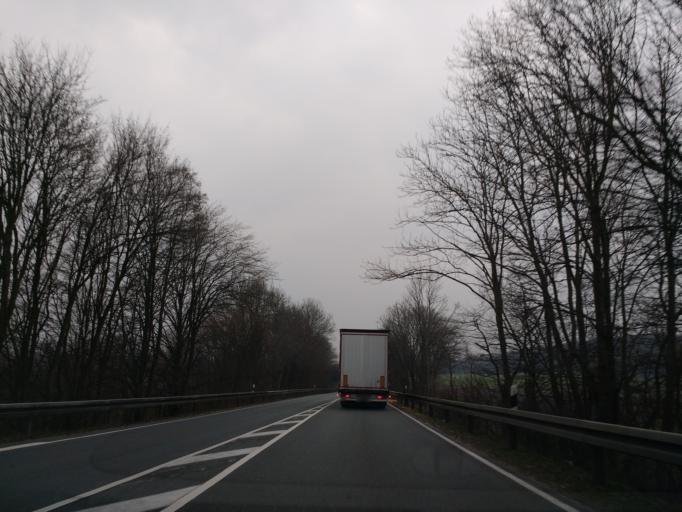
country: DE
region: North Rhine-Westphalia
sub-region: Regierungsbezirk Munster
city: Lotte
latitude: 52.2681
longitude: 7.8947
